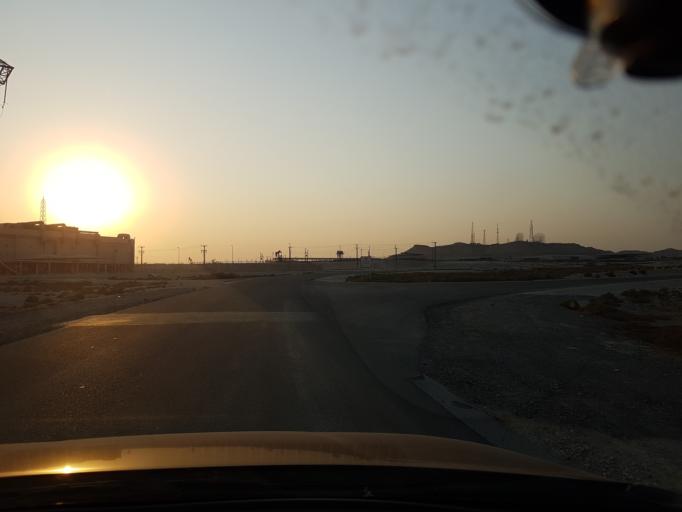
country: BH
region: Central Governorate
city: Dar Kulayb
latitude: 26.0188
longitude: 50.5591
